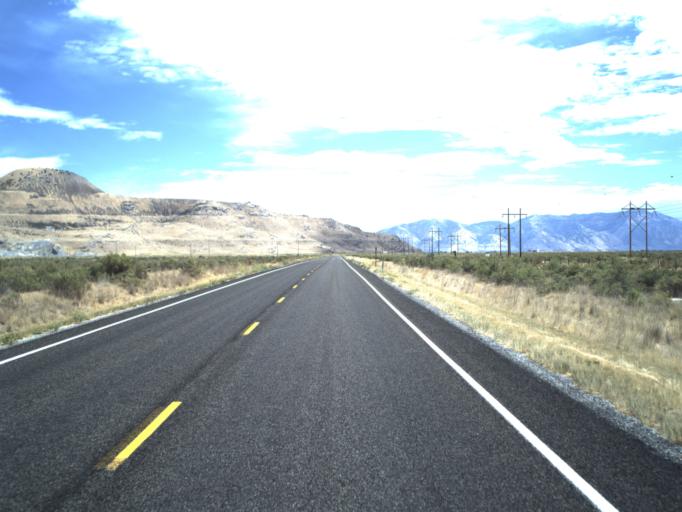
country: US
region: Utah
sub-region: Box Elder County
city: Tremonton
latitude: 41.6001
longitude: -112.3023
